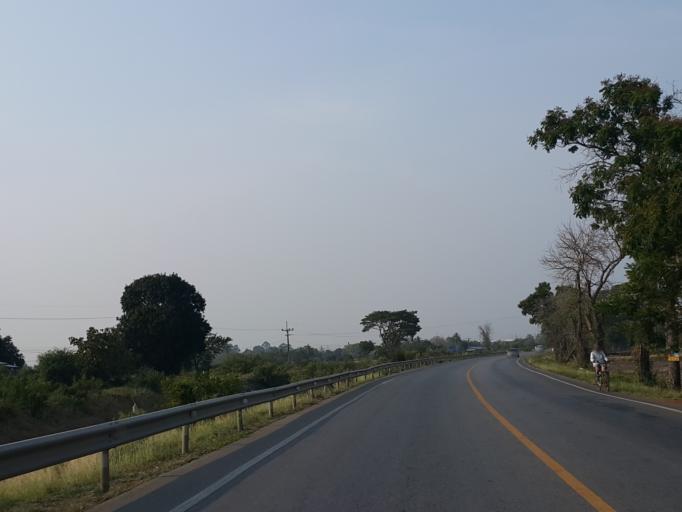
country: TH
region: Chai Nat
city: Sankhaburi
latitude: 15.0327
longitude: 100.1448
